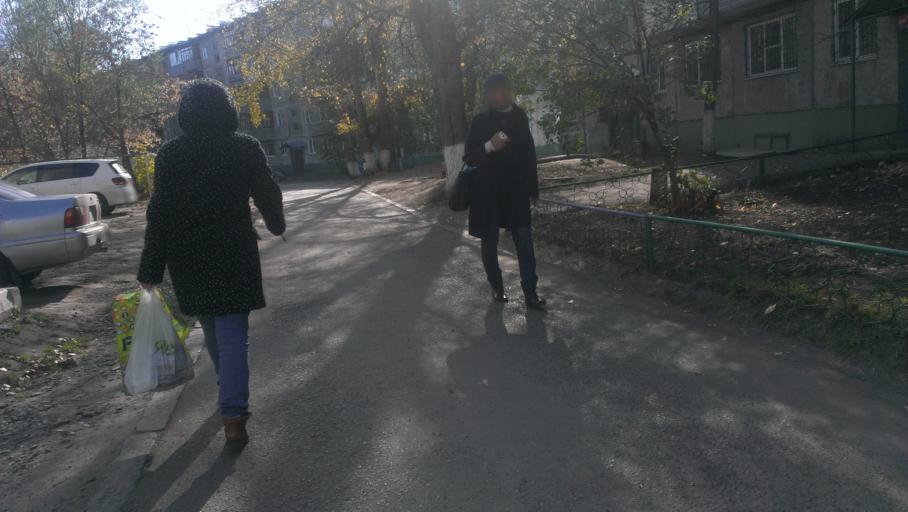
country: RU
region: Altai Krai
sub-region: Gorod Barnaulskiy
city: Barnaul
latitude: 53.3506
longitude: 83.6886
